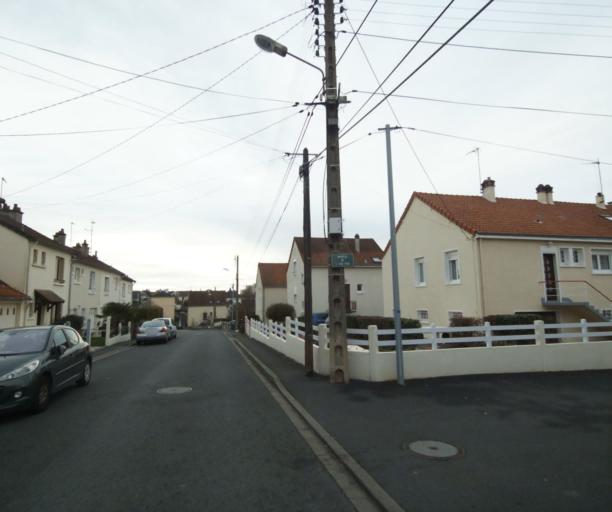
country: FR
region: Pays de la Loire
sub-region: Departement de la Sarthe
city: Coulaines
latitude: 48.0125
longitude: 0.2165
